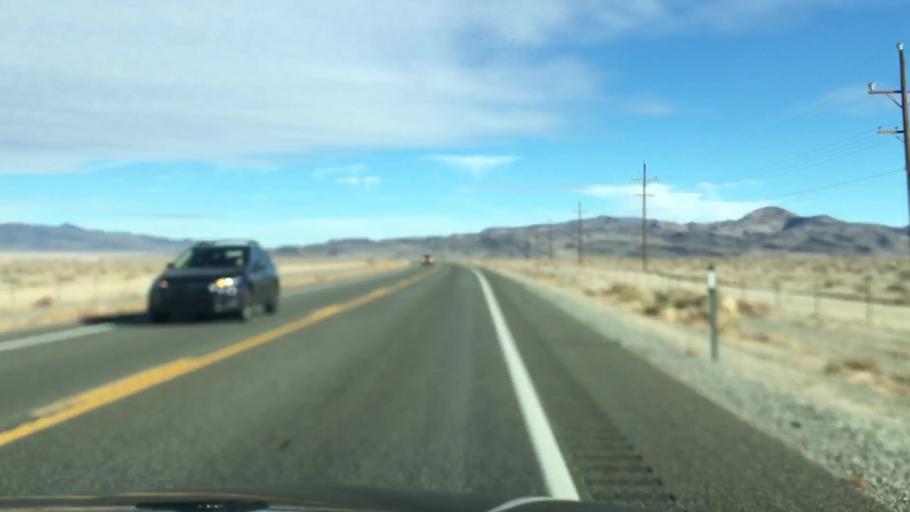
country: US
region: Nevada
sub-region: Mineral County
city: Hawthorne
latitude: 38.5246
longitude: -118.5814
